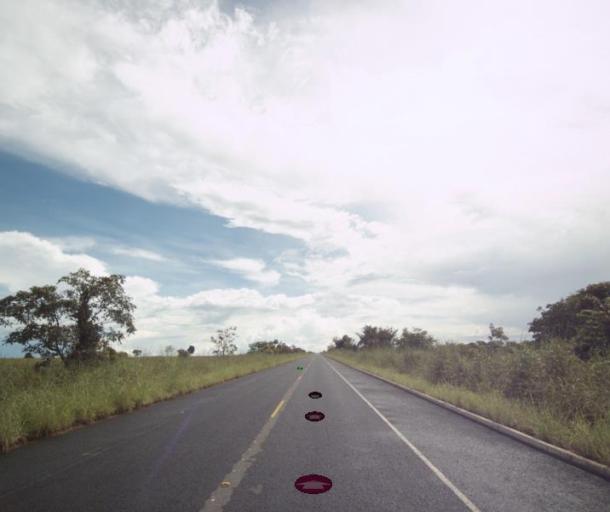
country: BR
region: Goias
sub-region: Sao Miguel Do Araguaia
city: Sao Miguel do Araguaia
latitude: -13.2975
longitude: -50.2449
